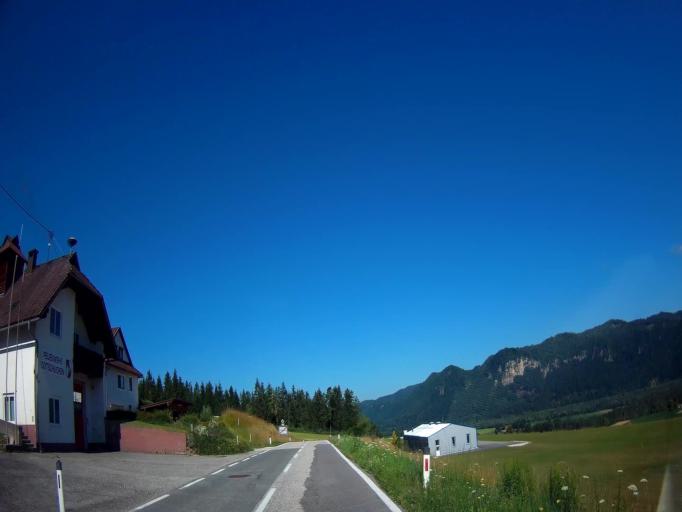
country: AT
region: Carinthia
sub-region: Politischer Bezirk Klagenfurt Land
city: Ebenthal
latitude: 46.5371
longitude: 14.3962
